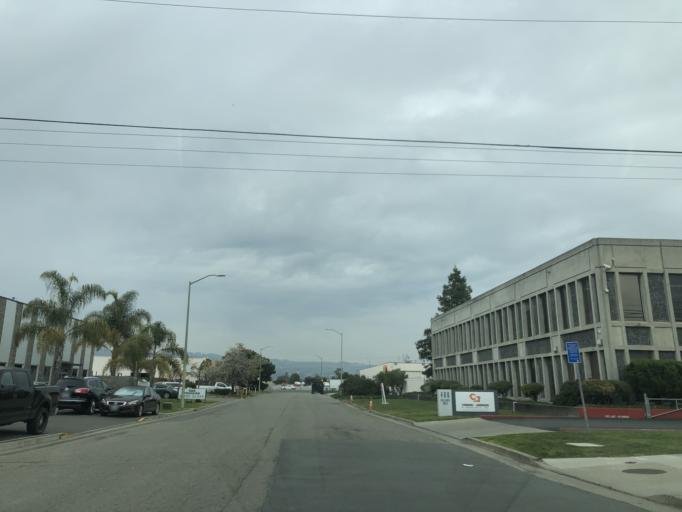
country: US
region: California
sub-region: Alameda County
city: Alameda
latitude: 37.7430
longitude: -122.2016
